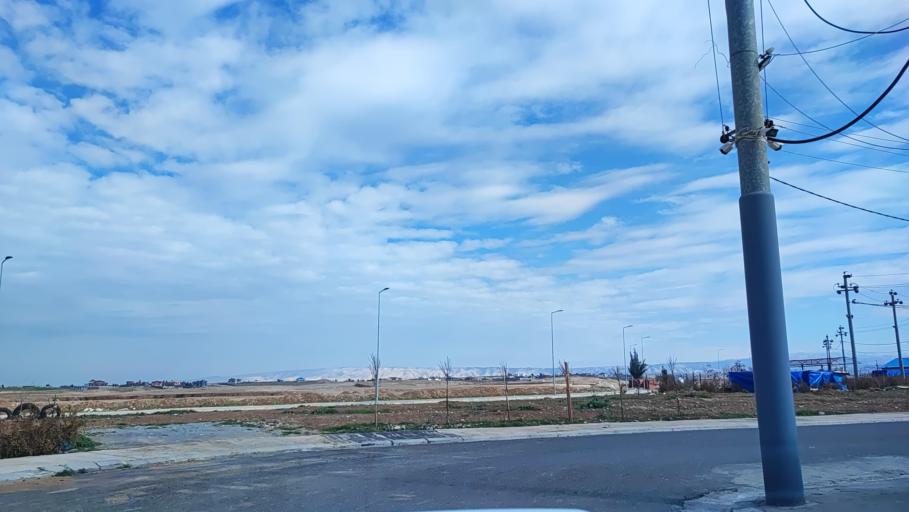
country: IQ
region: Arbil
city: Erbil
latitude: 36.2872
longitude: 44.0738
